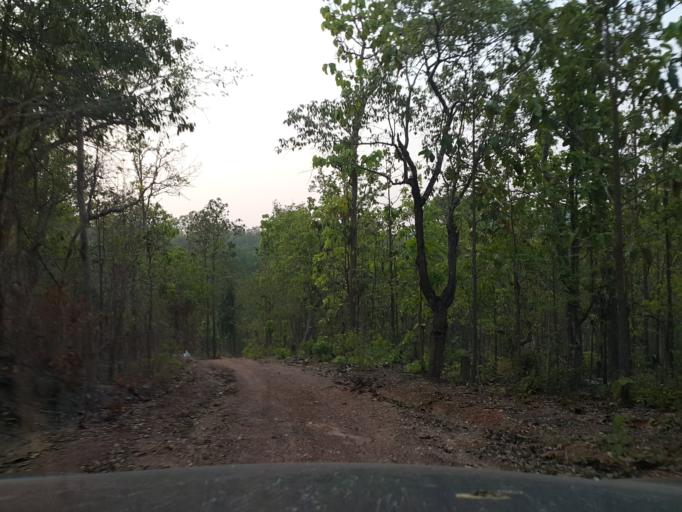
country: TH
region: Lamphun
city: Thung Hua Chang
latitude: 17.9086
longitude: 99.0809
